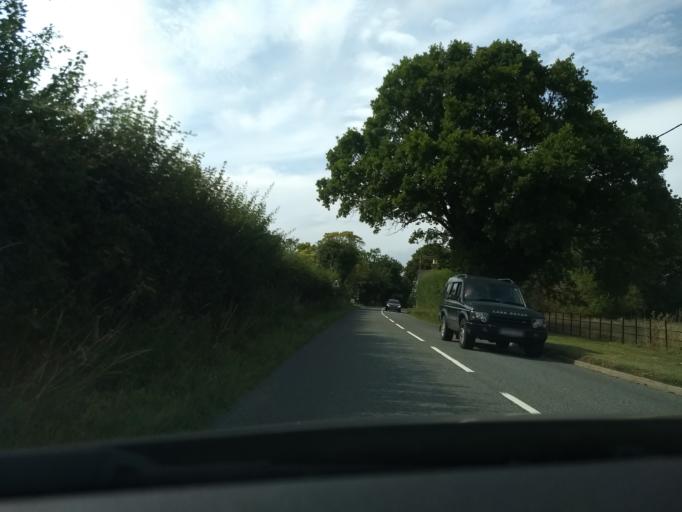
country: GB
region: England
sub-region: Suffolk
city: Ipswich
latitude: 51.9992
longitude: 1.1865
